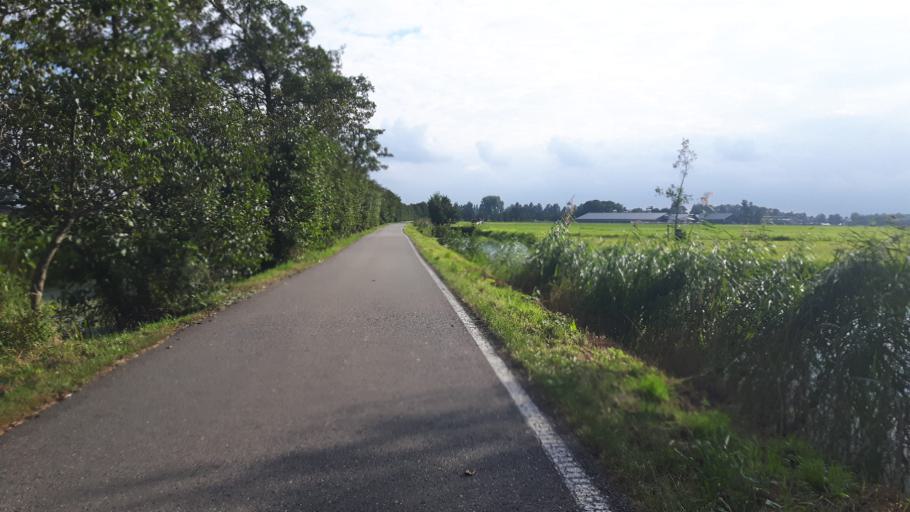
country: NL
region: Utrecht
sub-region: Gemeente De Ronde Venen
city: Mijdrecht
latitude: 52.1694
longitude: 4.9020
